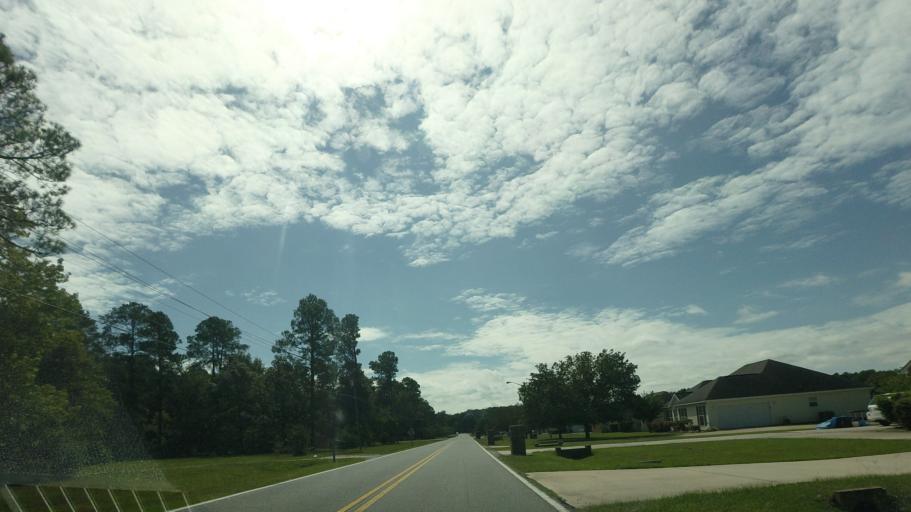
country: US
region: Georgia
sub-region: Houston County
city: Centerville
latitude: 32.5934
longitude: -83.7075
